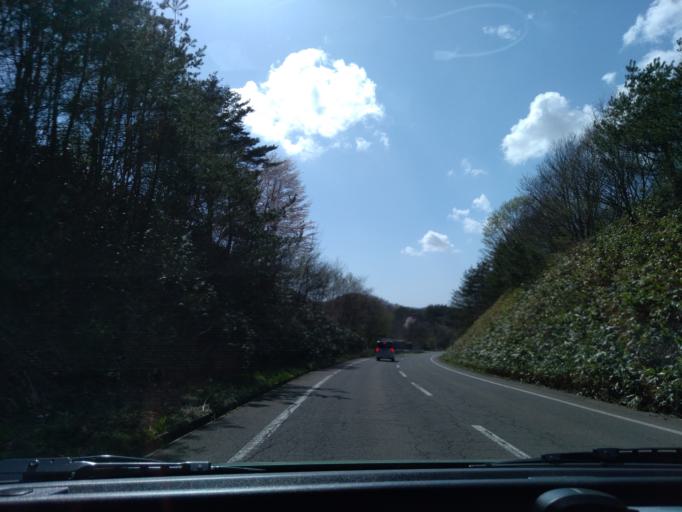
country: JP
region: Akita
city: Akita
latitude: 39.6934
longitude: 140.2449
